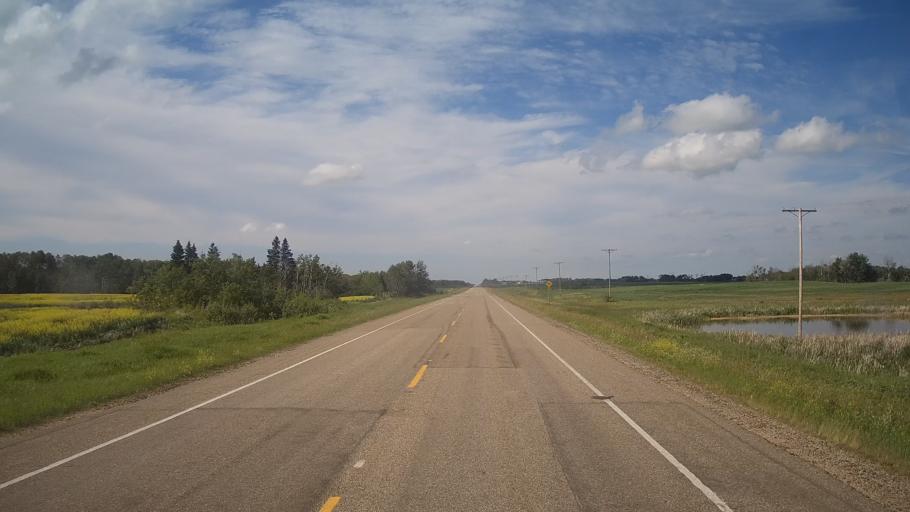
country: CA
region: Saskatchewan
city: Foam Lake
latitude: 51.5694
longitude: -103.8457
